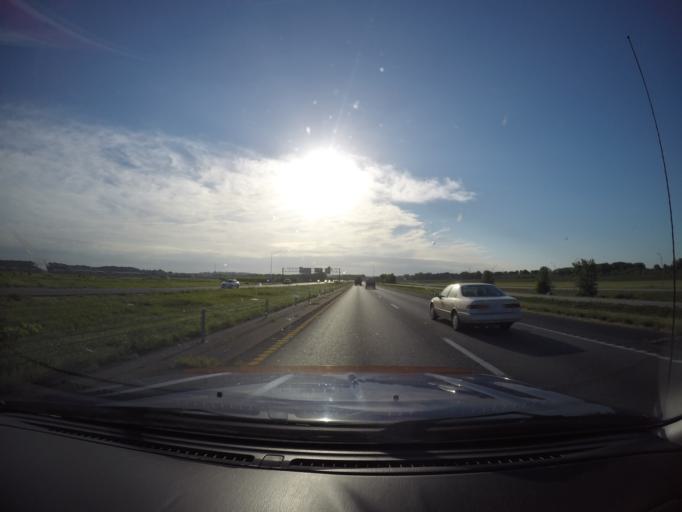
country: US
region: Missouri
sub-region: Platte County
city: Riverside
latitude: 39.1603
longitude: -94.6388
